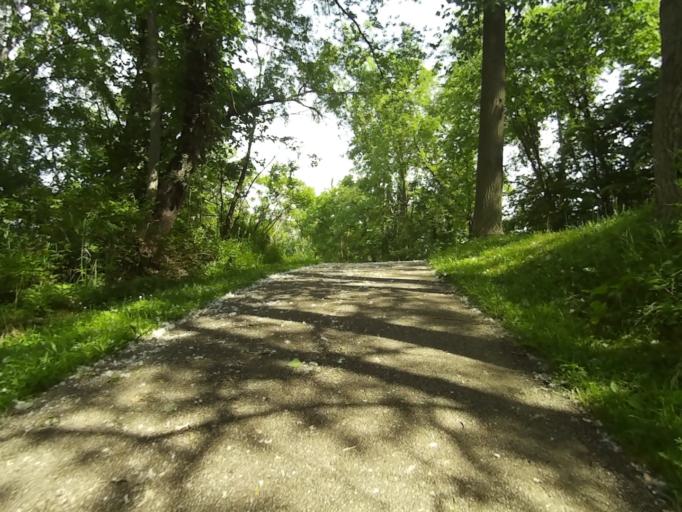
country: US
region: Ohio
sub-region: Summit County
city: Hudson
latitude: 41.2182
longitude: -81.4717
